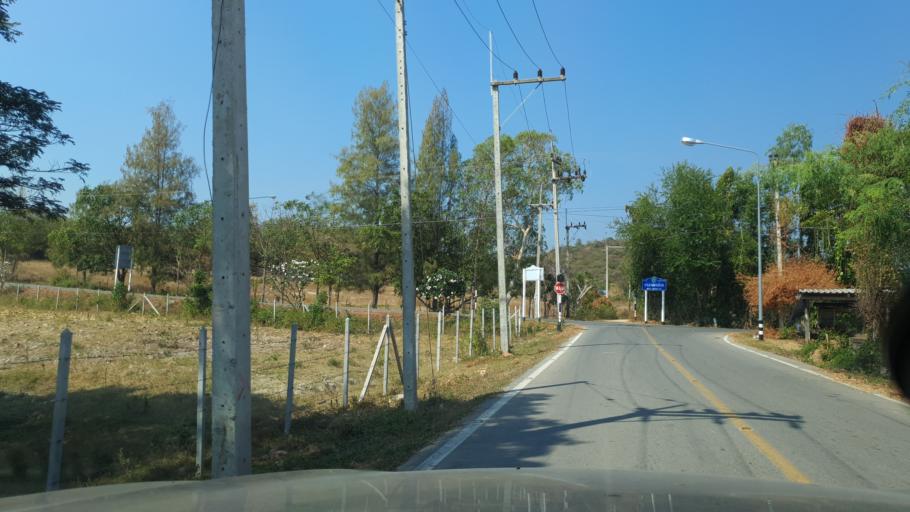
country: TH
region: Prachuap Khiri Khan
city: Sam Roi Yot
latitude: 12.2855
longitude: 99.9715
